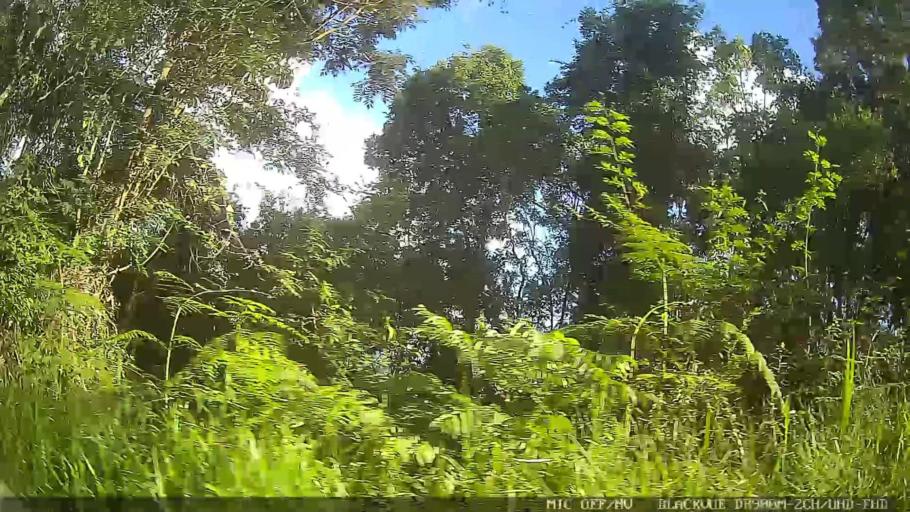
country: BR
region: Minas Gerais
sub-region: Extrema
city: Extrema
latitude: -22.8252
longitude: -46.2535
